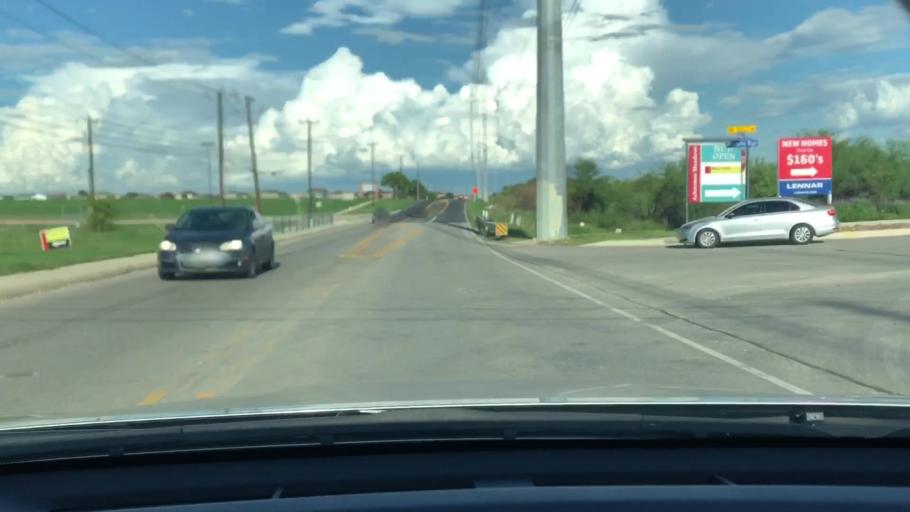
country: US
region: Texas
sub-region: Bexar County
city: Kirby
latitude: 29.4669
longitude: -98.3435
